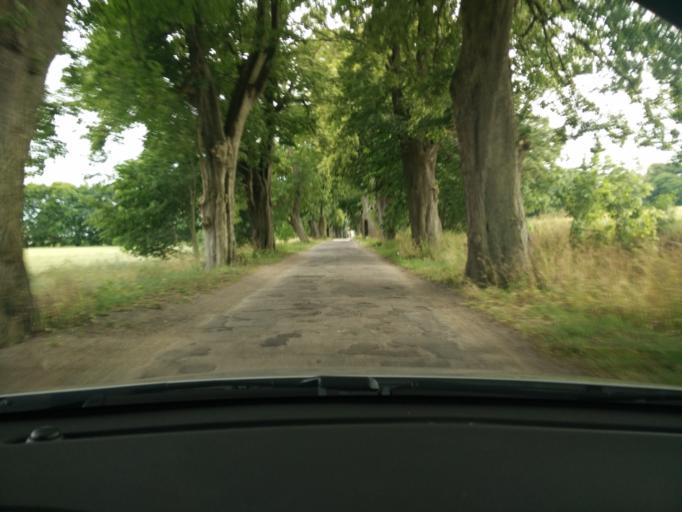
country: PL
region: Pomeranian Voivodeship
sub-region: Powiat pucki
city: Mrzezino
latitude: 54.6716
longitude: 18.4576
